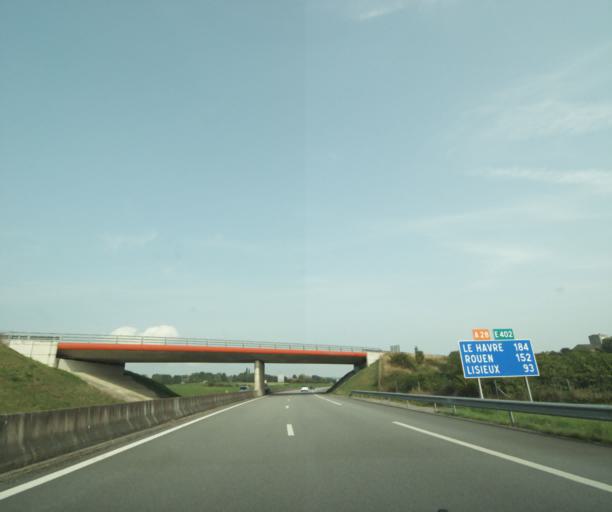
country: FR
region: Lower Normandy
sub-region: Departement de l'Orne
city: Valframbert
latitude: 48.4595
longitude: 0.1255
